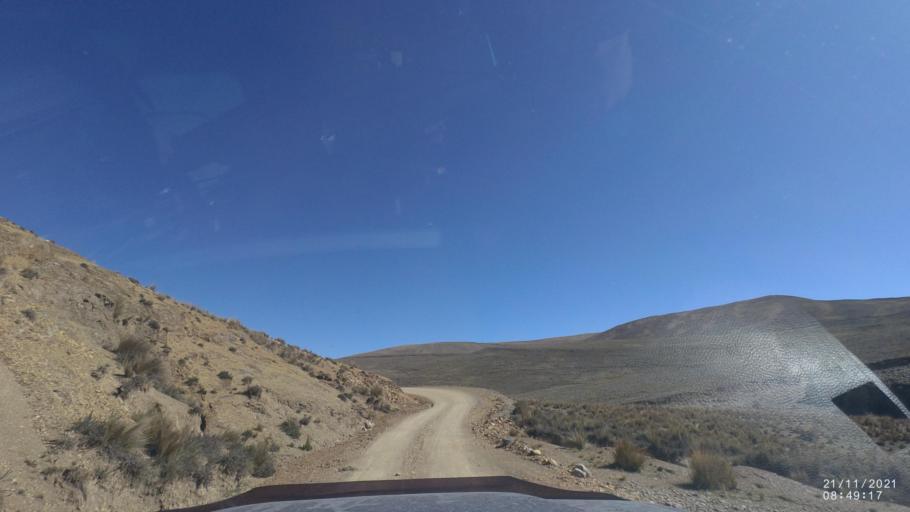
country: BO
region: Cochabamba
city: Cochabamba
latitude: -17.2252
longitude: -66.2318
